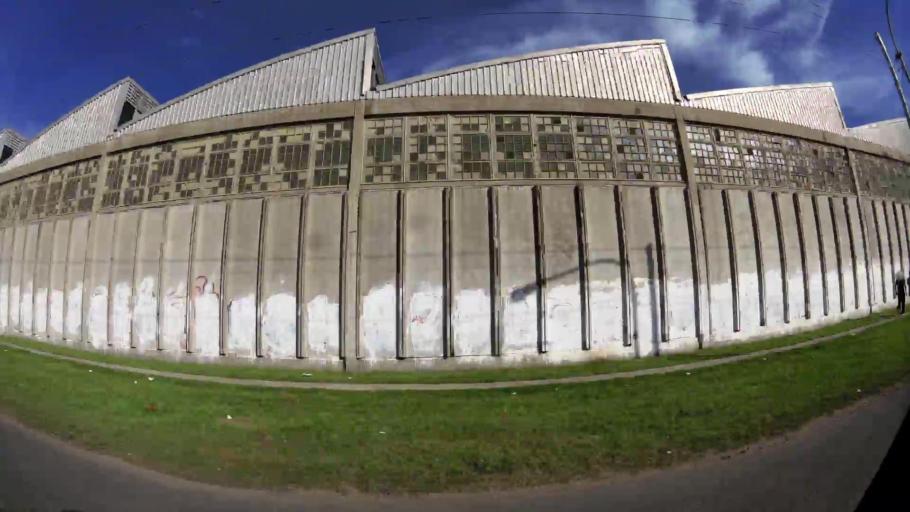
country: AR
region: Buenos Aires
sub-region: Partido de Quilmes
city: Quilmes
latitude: -34.7996
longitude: -58.2177
